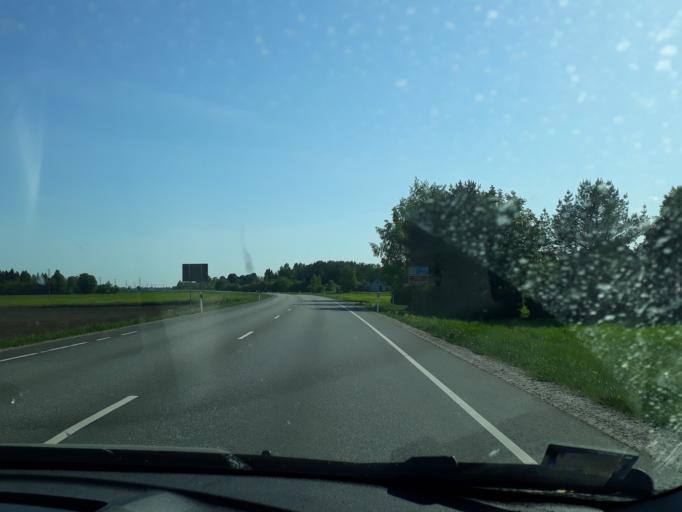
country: EE
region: Paernumaa
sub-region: Tootsi vald
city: Tootsi
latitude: 58.5730
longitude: 24.8790
